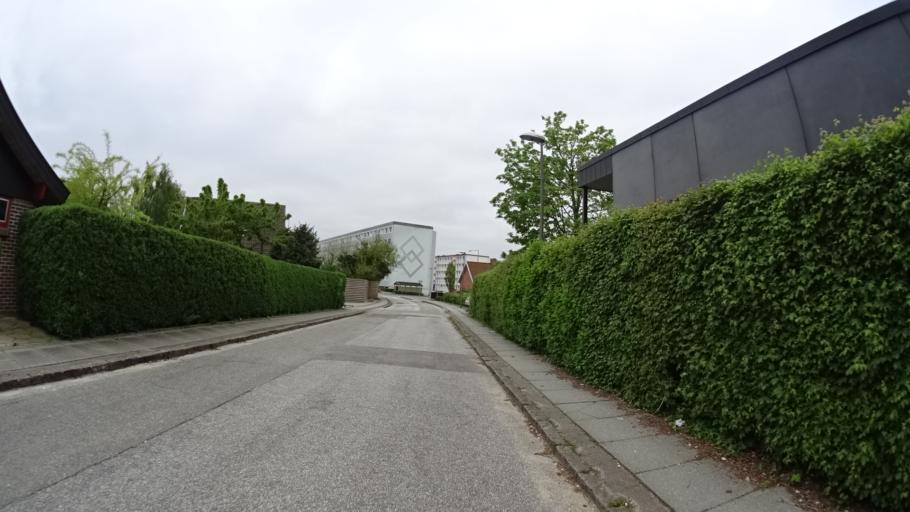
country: DK
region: Central Jutland
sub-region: Arhus Kommune
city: Arhus
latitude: 56.1313
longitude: 10.1763
